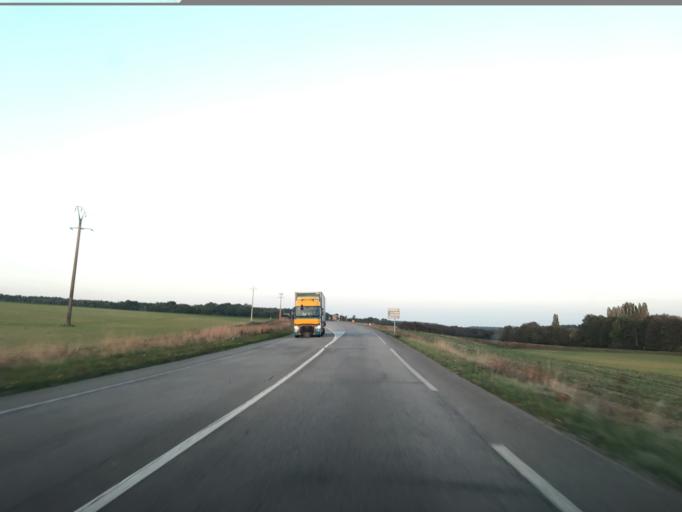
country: FR
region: Haute-Normandie
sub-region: Departement de l'Eure
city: Bourth
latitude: 48.7062
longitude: 0.8450
